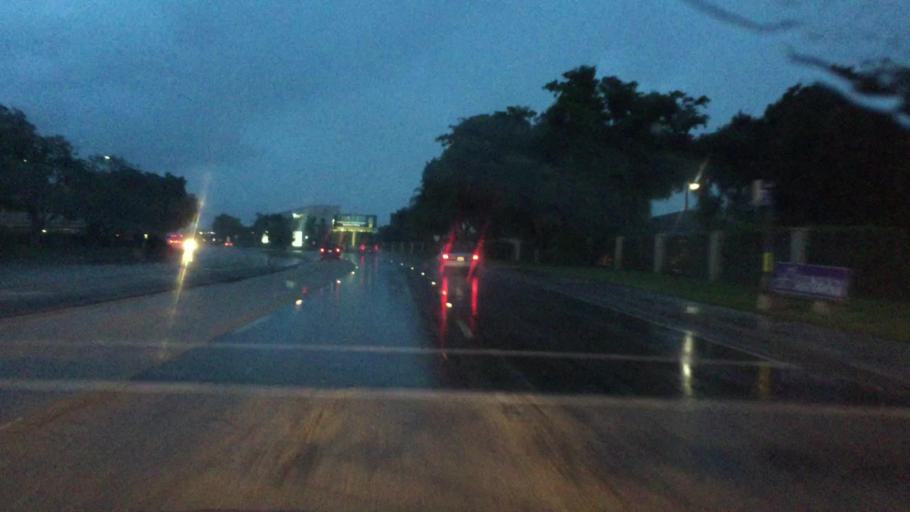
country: US
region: Florida
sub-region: Lee County
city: Villas
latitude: 26.5566
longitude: -81.8811
